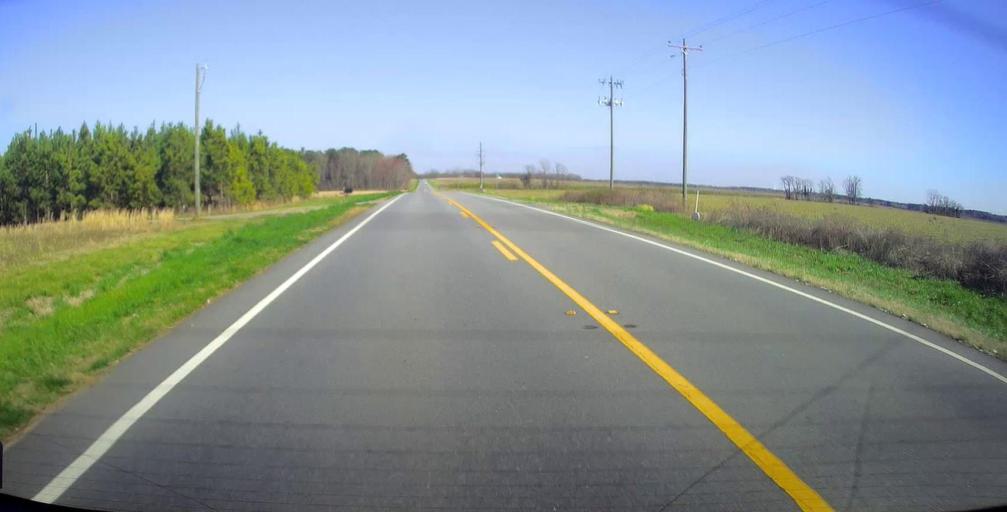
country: US
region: Georgia
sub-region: Dooly County
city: Unadilla
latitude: 32.3379
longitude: -83.8318
